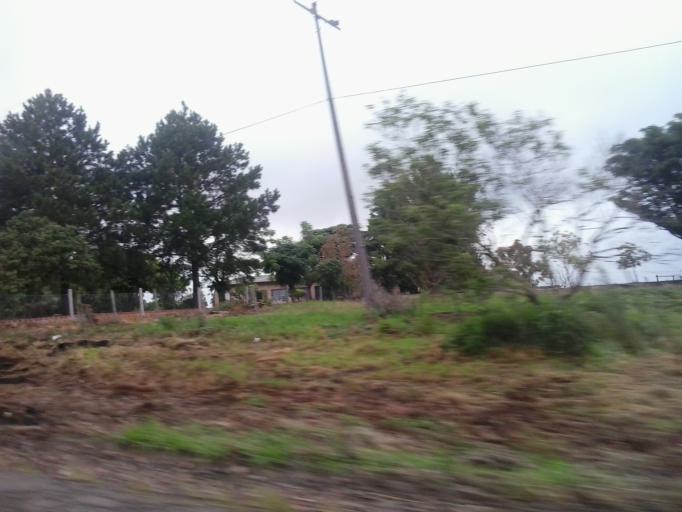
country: BR
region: Rio Grande do Sul
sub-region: Santa Maria
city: Santa Maria
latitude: -29.7228
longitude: -53.3900
